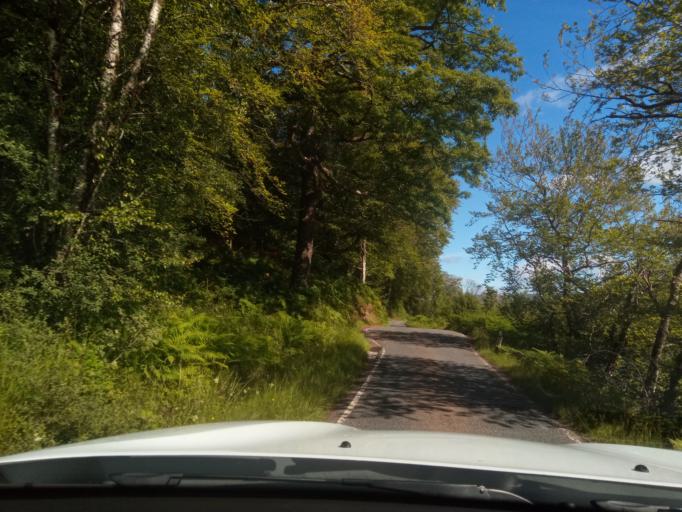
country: GB
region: Scotland
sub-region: Argyll and Bute
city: Isle Of Mull
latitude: 56.7316
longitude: -5.7773
